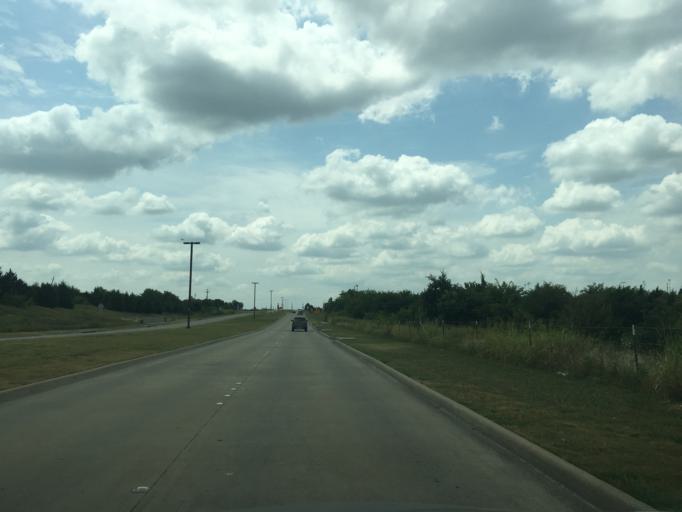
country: US
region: Texas
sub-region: Rockwall County
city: Rockwall
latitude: 32.9289
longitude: -96.4373
